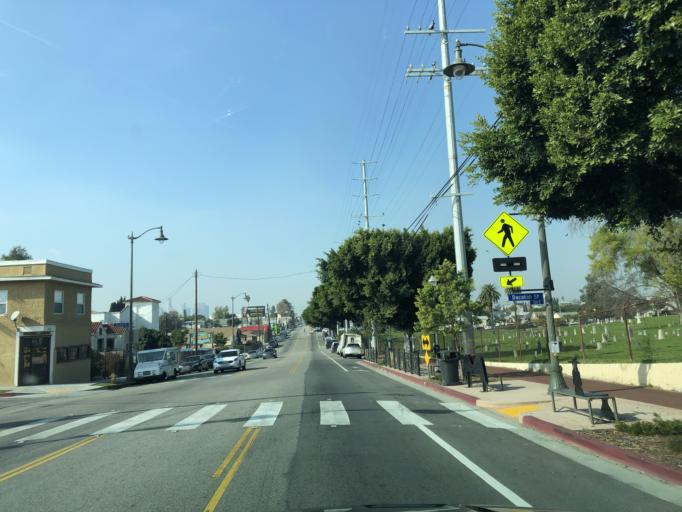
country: US
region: California
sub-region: Los Angeles County
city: Boyle Heights
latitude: 34.0394
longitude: -118.2000
